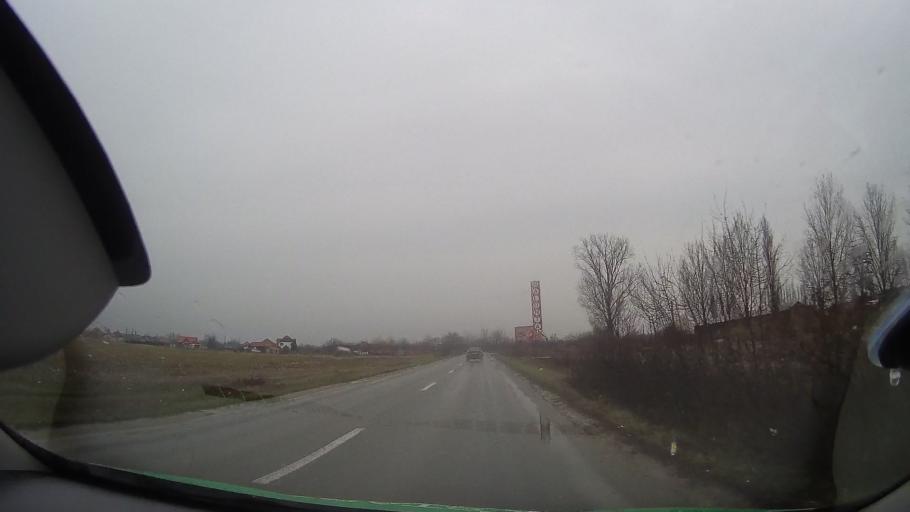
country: RO
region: Bihor
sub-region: Municipiul Salonta
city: Salonta
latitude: 46.7946
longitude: 21.6849
